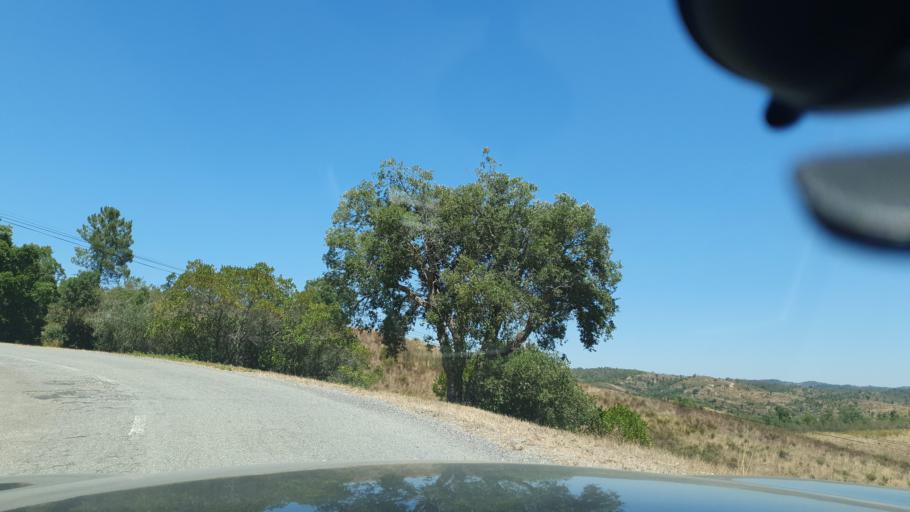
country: PT
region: Beja
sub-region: Odemira
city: Odemira
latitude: 37.6067
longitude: -8.4965
